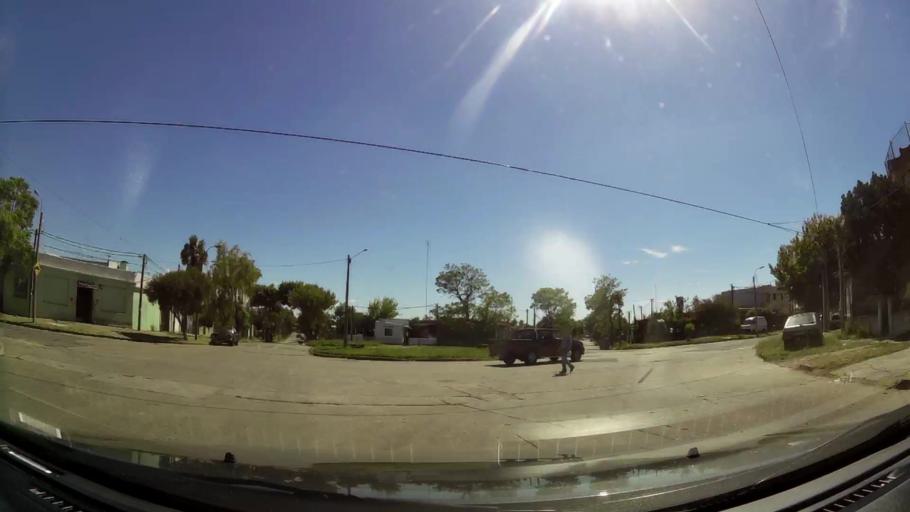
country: UY
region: Montevideo
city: Montevideo
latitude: -34.8639
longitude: -56.1260
